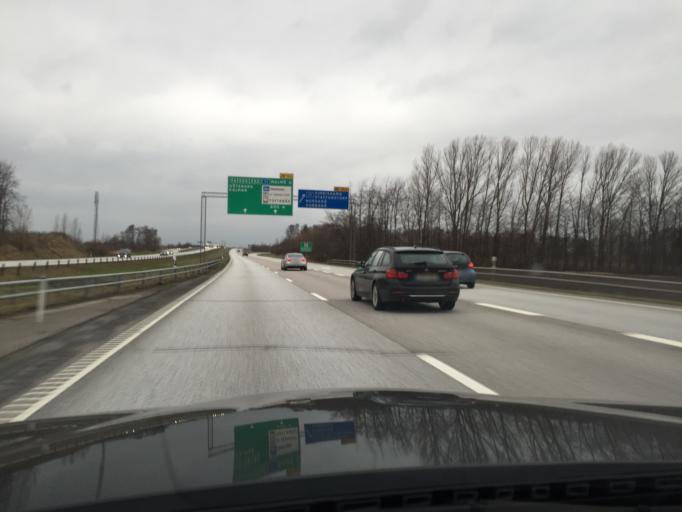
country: SE
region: Skane
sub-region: Burlovs Kommun
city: Arloev
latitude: 55.6065
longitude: 13.1165
